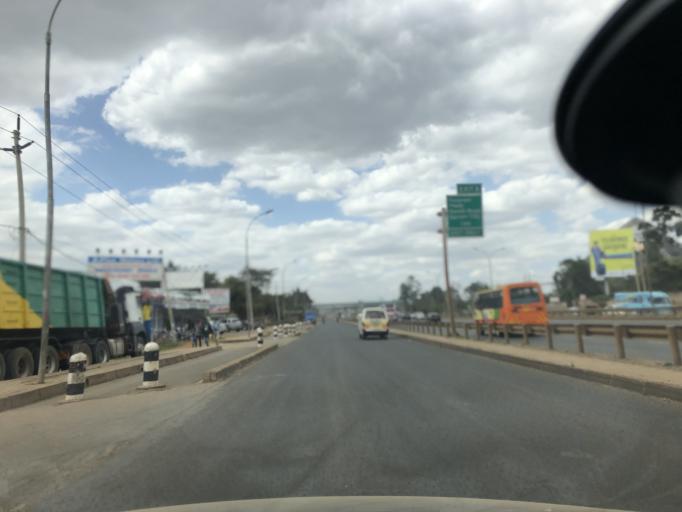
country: KE
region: Nairobi Area
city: Pumwani
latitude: -1.2279
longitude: 36.8815
